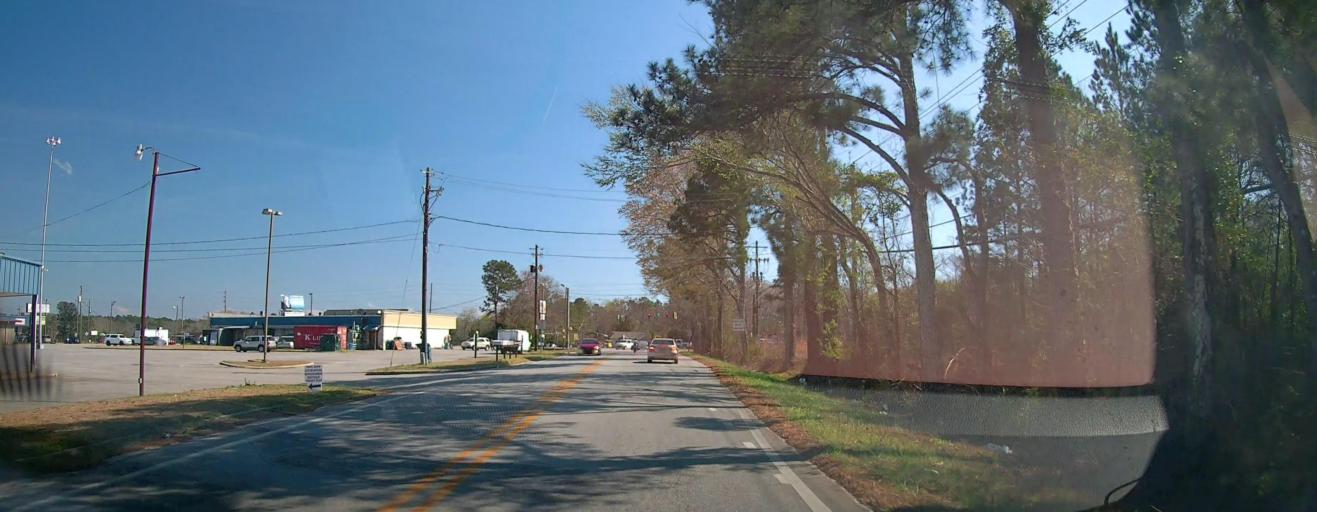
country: US
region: Georgia
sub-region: Bibb County
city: Macon
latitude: 32.8733
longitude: -83.5605
